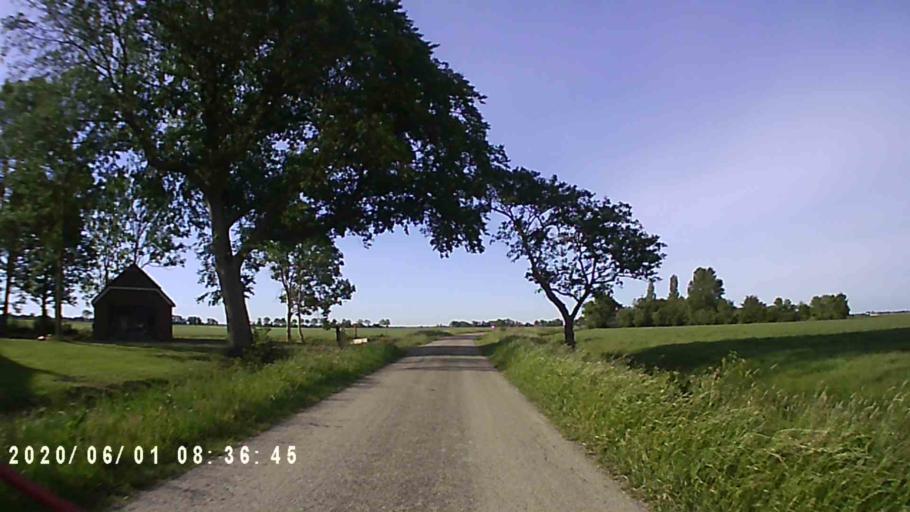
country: NL
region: Friesland
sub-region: Gemeente Ferwerderadiel
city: Burdaard
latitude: 53.2981
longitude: 5.8454
